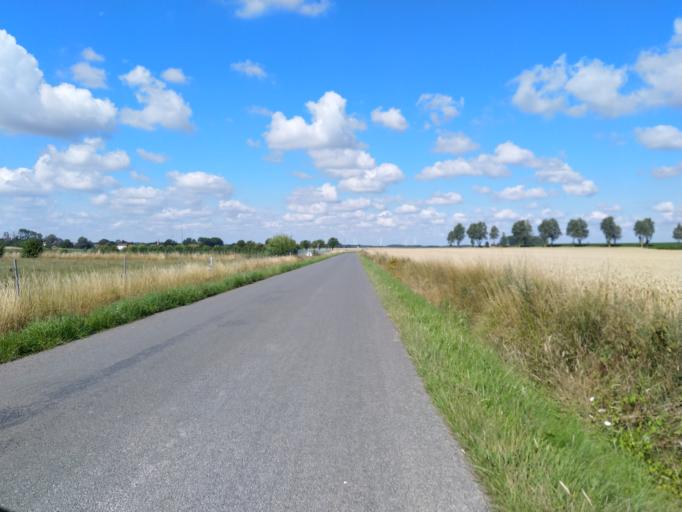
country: BE
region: Wallonia
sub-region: Province du Hainaut
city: Beloeil
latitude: 50.5934
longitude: 3.7354
